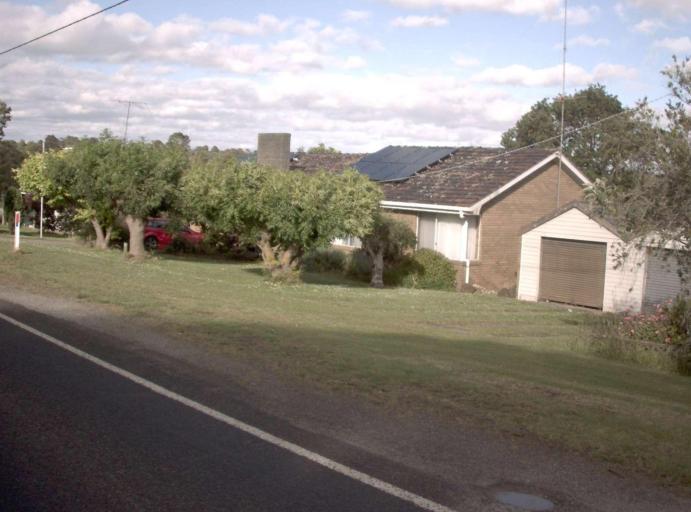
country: AU
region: Victoria
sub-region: Baw Baw
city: Warragul
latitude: -38.4857
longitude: 145.9366
